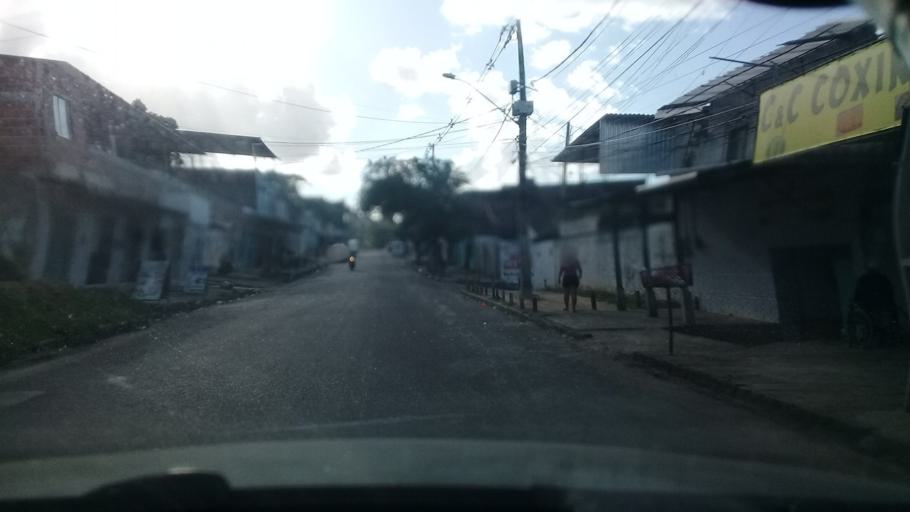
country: BR
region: Pernambuco
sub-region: Jaboatao Dos Guararapes
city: Jaboatao dos Guararapes
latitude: -8.1190
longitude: -34.9402
